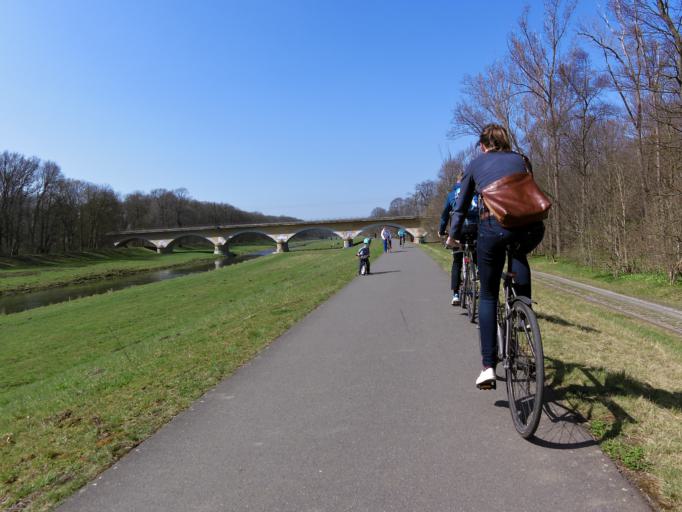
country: DE
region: Saxony
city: Leipzig
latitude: 51.3670
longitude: 12.3265
